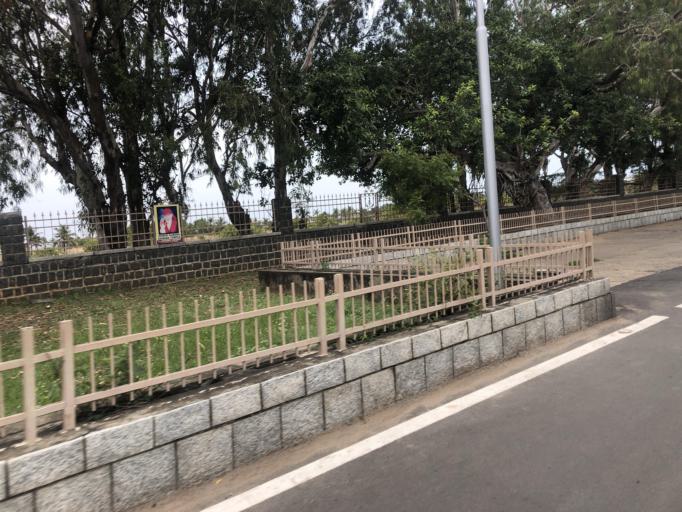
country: IN
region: Tamil Nadu
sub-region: Kancheepuram
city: Mamallapuram
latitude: 12.6114
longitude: 80.1904
